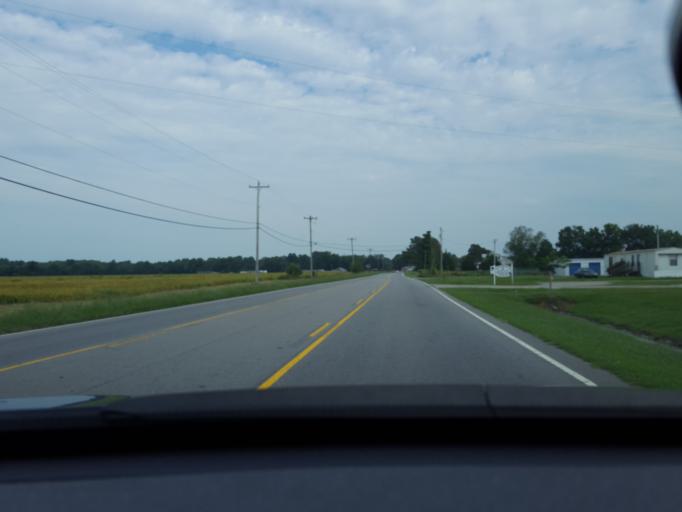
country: US
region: North Carolina
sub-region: Chowan County
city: Edenton
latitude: 36.0918
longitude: -76.6293
